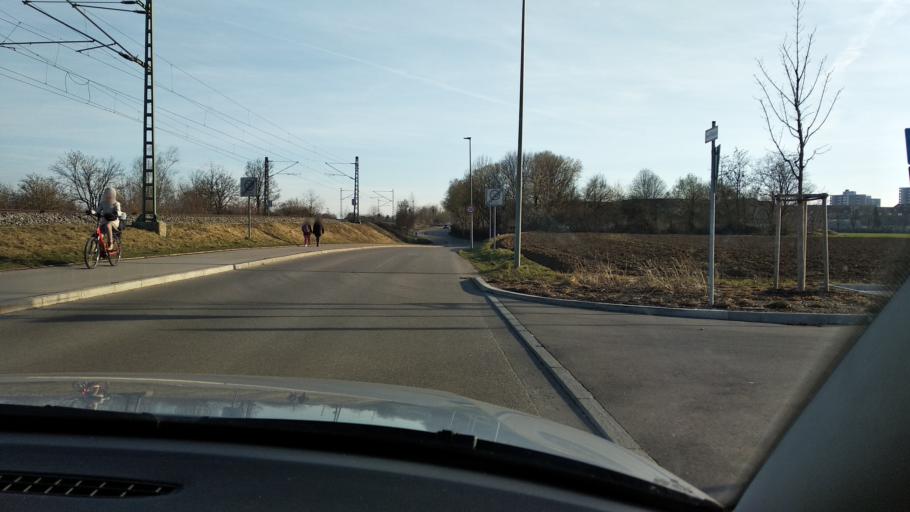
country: DE
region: Bavaria
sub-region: Upper Bavaria
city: Unterhaching
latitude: 48.0599
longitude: 11.6119
